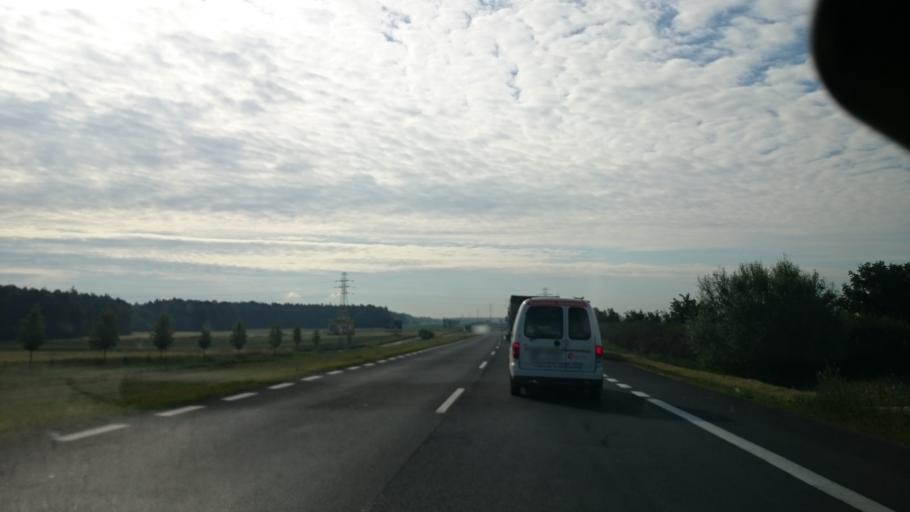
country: PL
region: Opole Voivodeship
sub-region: Powiat opolski
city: Opole
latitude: 50.6940
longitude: 17.9632
